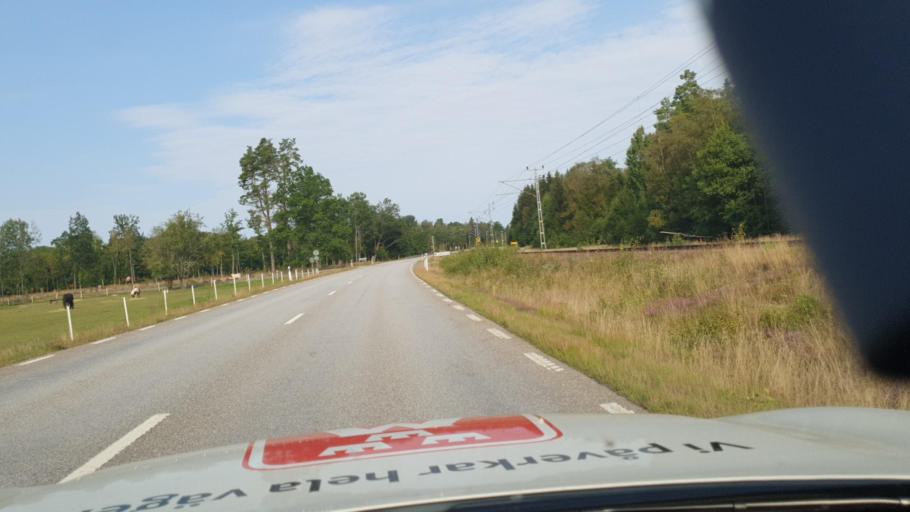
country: SE
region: Vaestra Goetaland
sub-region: Bengtsfors Kommun
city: Dals Langed
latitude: 58.7928
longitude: 12.1713
